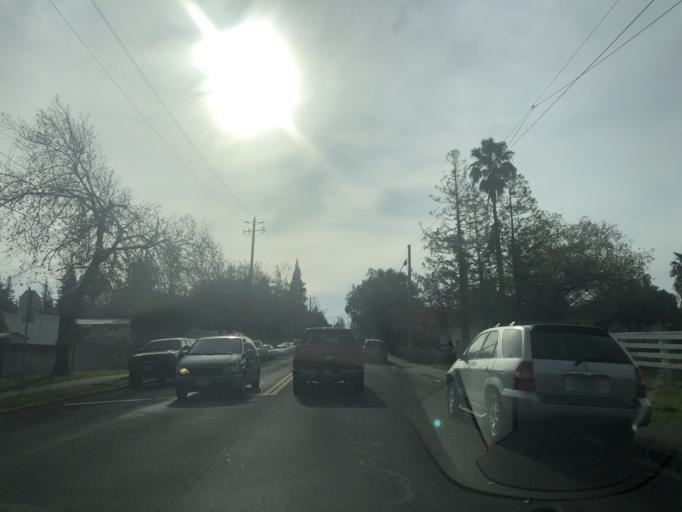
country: US
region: California
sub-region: Contra Costa County
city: Concord
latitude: 37.9962
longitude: -122.0424
